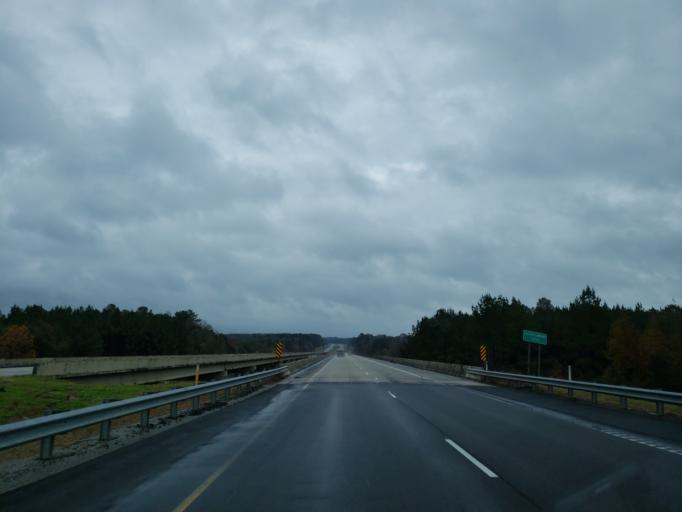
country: US
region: Mississippi
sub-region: Clarke County
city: Quitman
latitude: 31.9814
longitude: -88.7195
